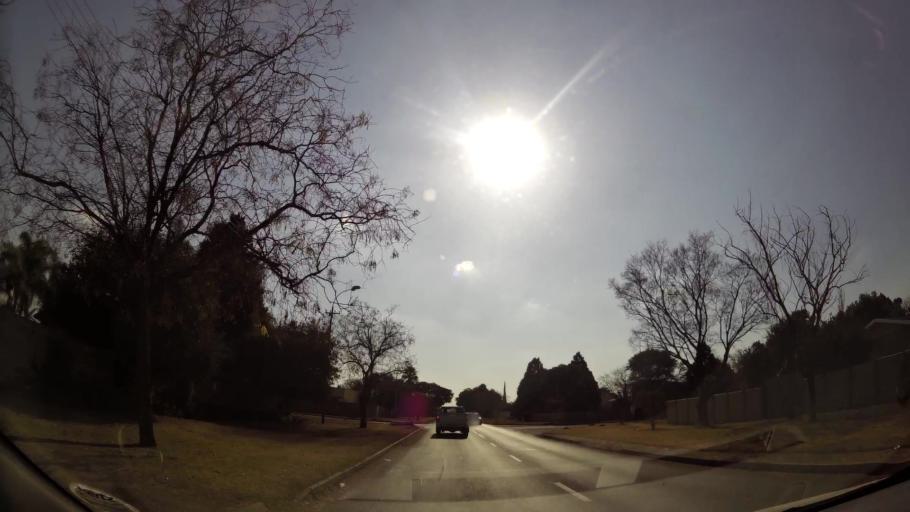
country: ZA
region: Gauteng
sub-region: West Rand District Municipality
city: Randfontein
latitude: -26.1587
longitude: 27.7025
